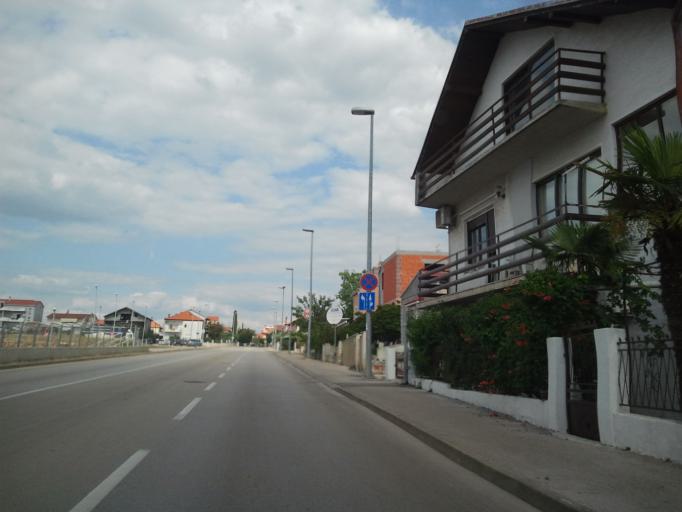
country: HR
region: Zadarska
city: Zadar
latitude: 44.1190
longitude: 15.2463
